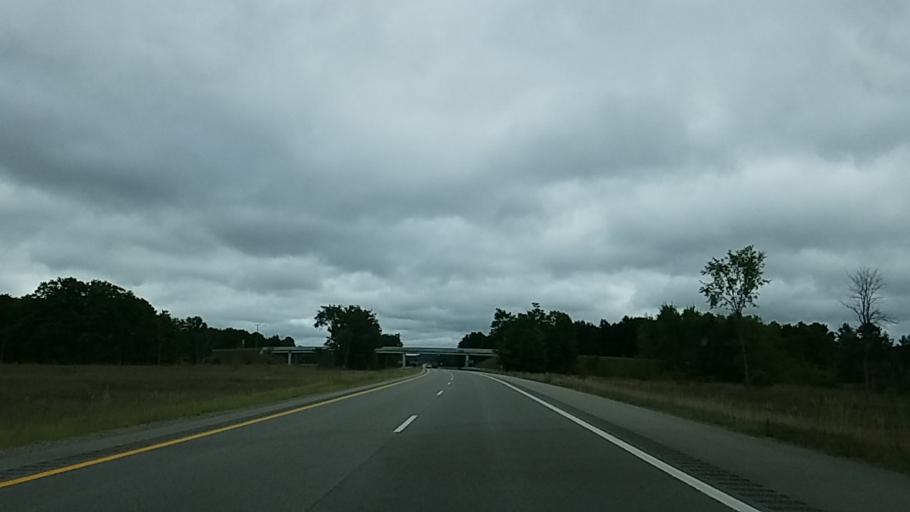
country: US
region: Michigan
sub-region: Otsego County
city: Gaylord
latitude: 45.1518
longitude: -84.6699
